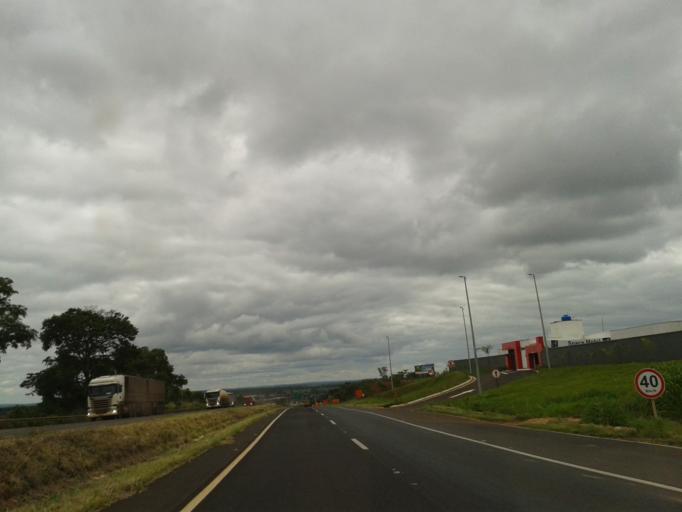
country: BR
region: Minas Gerais
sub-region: Monte Alegre De Minas
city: Monte Alegre de Minas
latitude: -18.8585
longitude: -48.8594
